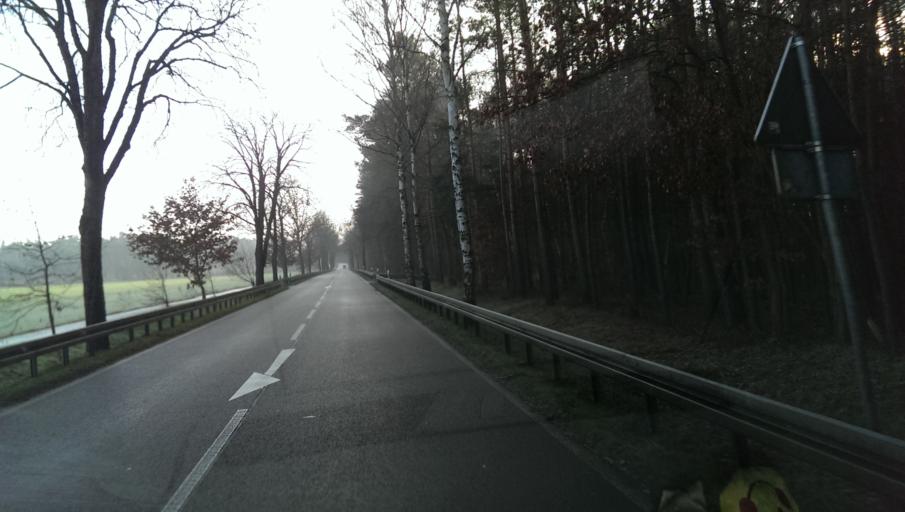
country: DE
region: Brandenburg
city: Schilda
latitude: 51.5630
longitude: 13.3656
